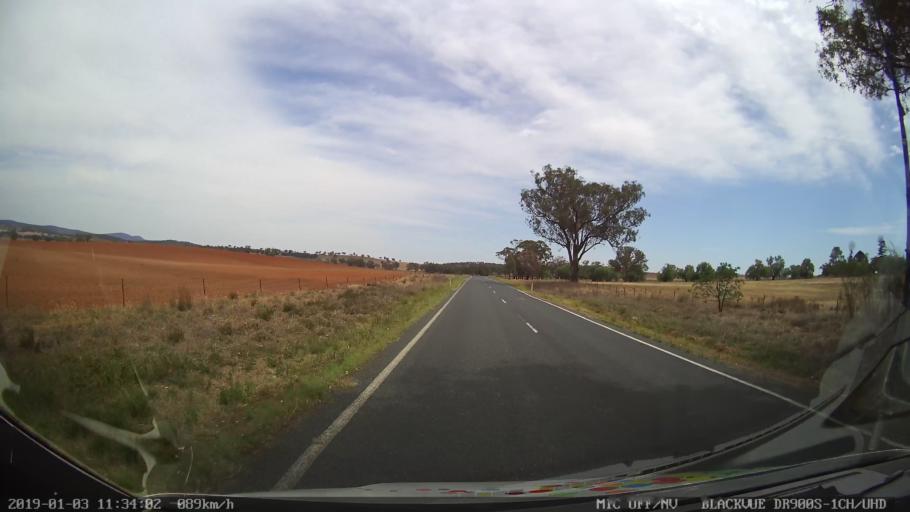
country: AU
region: New South Wales
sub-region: Weddin
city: Grenfell
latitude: -33.9397
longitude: 148.1667
